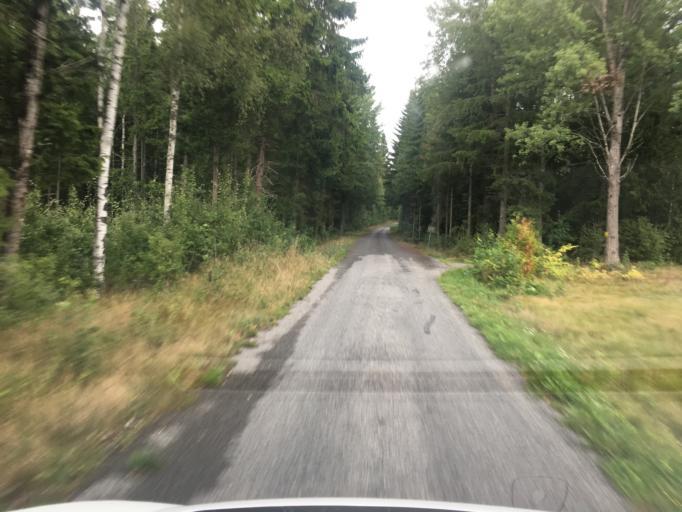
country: SE
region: Kronoberg
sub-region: Ljungby Kommun
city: Lagan
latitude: 56.9518
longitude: 14.0366
